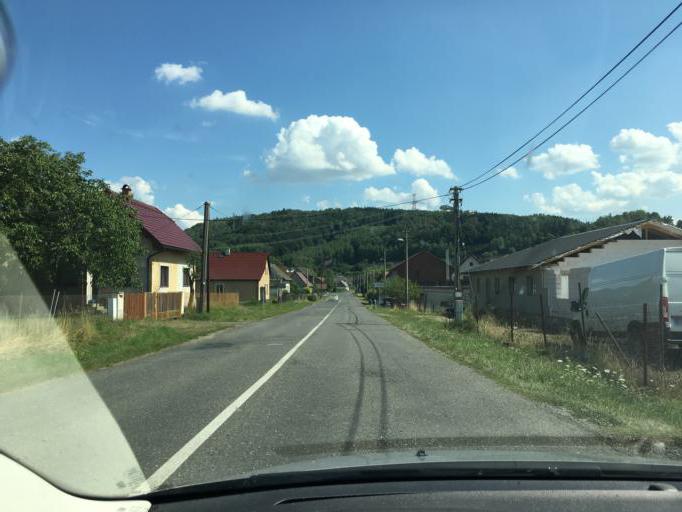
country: CZ
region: Liberecky
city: Hodkovice nad Mohelkou
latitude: 50.6565
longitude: 15.1049
